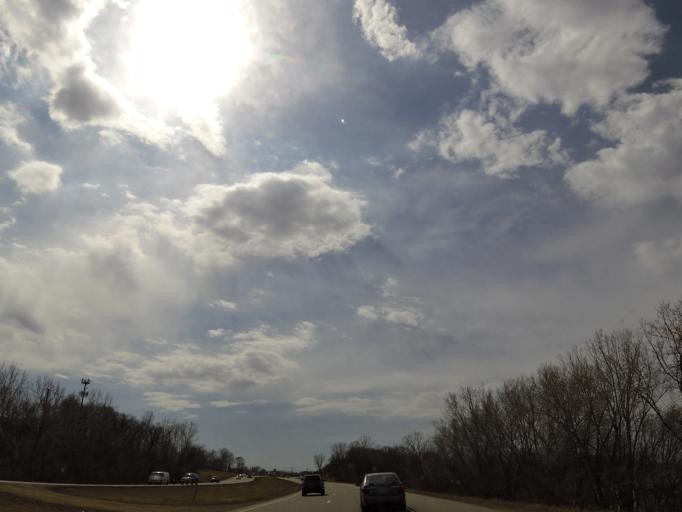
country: US
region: Minnesota
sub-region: Dakota County
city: Eagan
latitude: 44.8104
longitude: -93.2273
